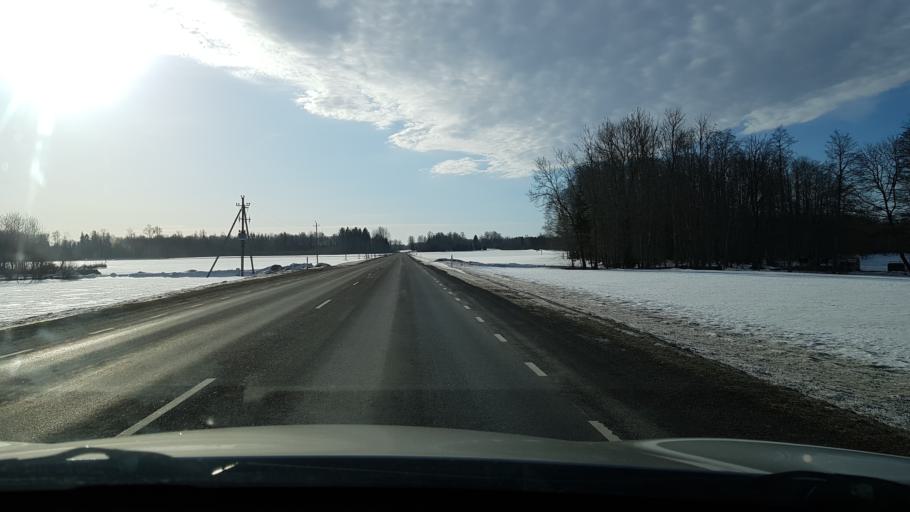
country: EE
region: Viljandimaa
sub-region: Viljandi linn
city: Viljandi
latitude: 58.4563
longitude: 25.5938
